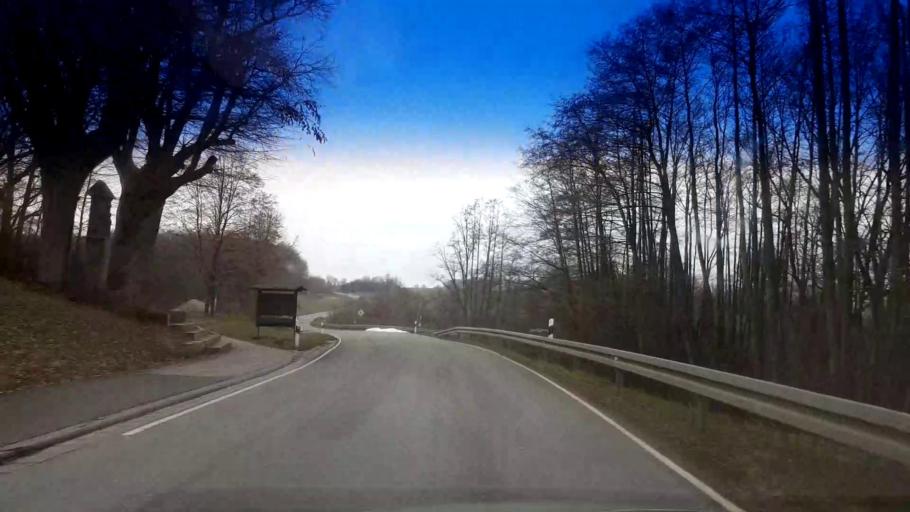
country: DE
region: Bavaria
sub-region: Upper Franconia
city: Altendorf
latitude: 49.7961
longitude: 10.9948
